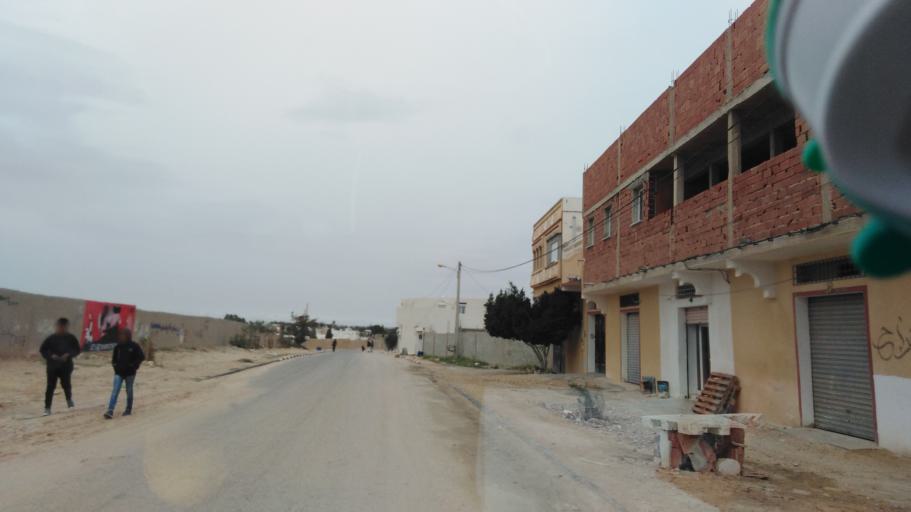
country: TN
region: Qabis
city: Gabes
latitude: 33.9542
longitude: 10.0031
